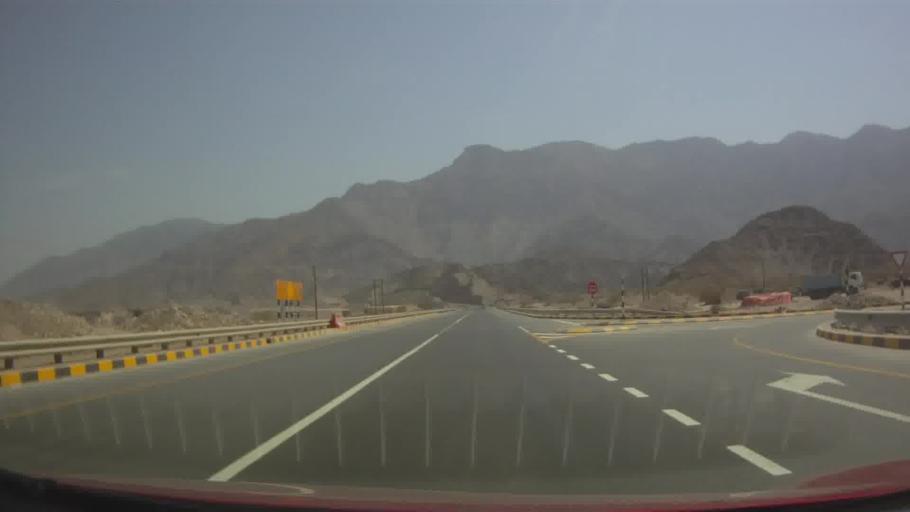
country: OM
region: Muhafazat Masqat
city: Muscat
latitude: 23.4051
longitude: 58.7805
